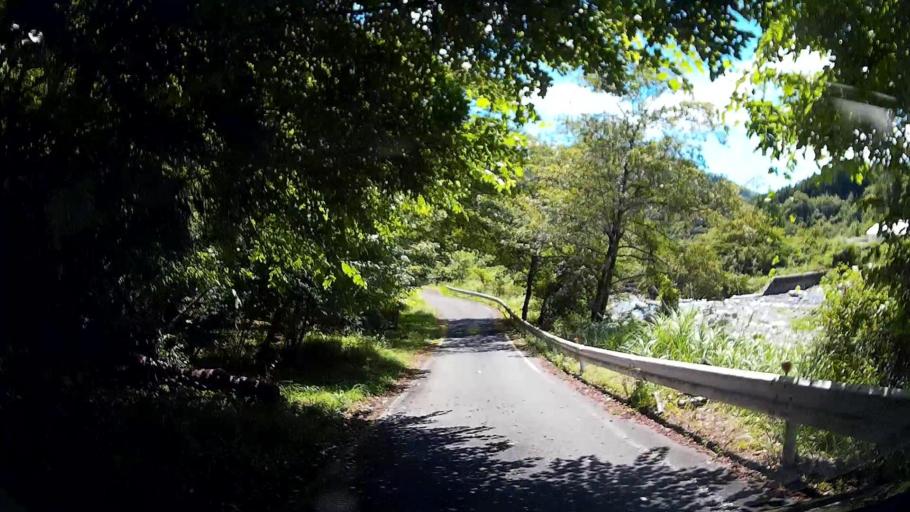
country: JP
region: Shizuoka
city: Fujinomiya
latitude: 35.2825
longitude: 138.3280
